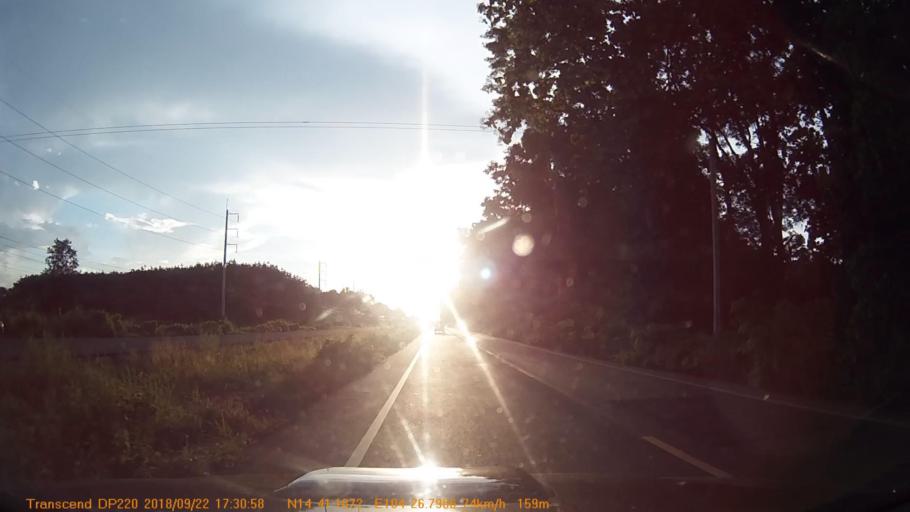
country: TH
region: Sisaket
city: Khun Han
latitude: 14.6865
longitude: 104.4460
